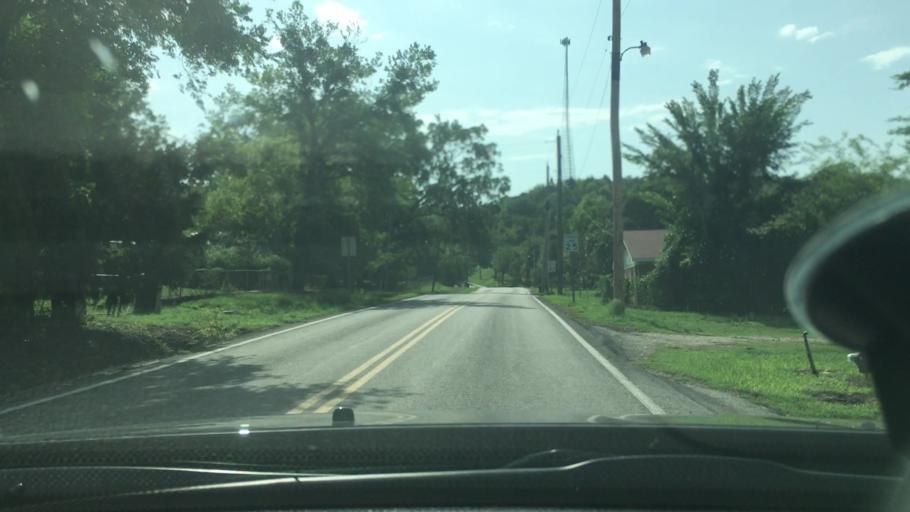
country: US
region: Oklahoma
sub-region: Atoka County
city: Atoka
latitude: 34.4689
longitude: -96.0524
